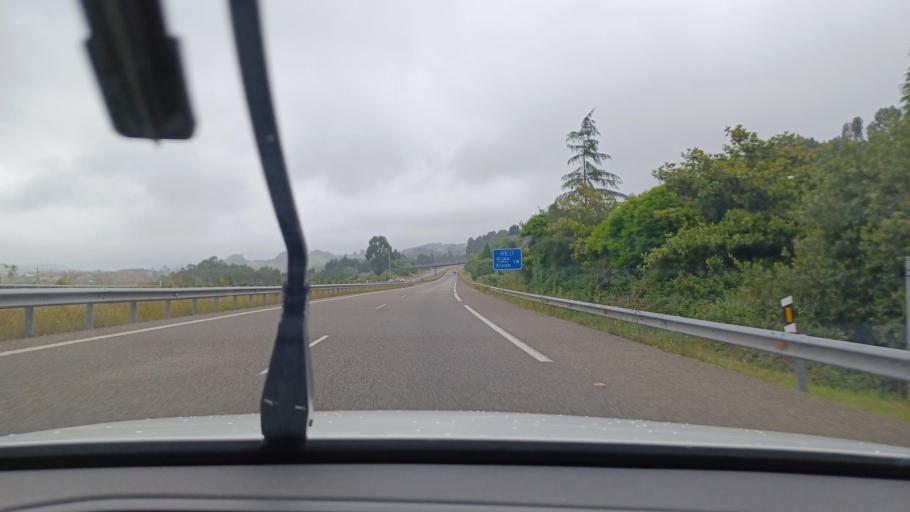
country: ES
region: Asturias
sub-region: Province of Asturias
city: Lugones
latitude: 43.4539
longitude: -5.7903
